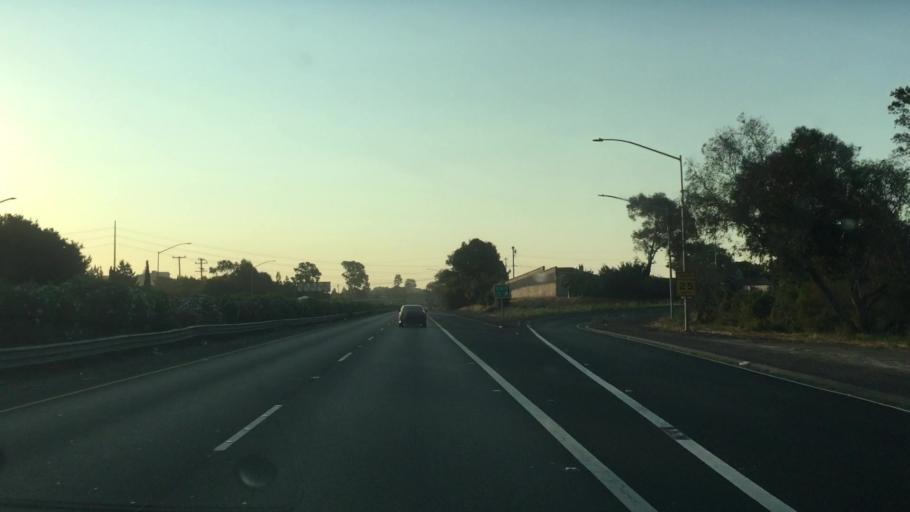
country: US
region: California
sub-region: Solano County
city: Vallejo
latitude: 38.0906
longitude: -122.2271
